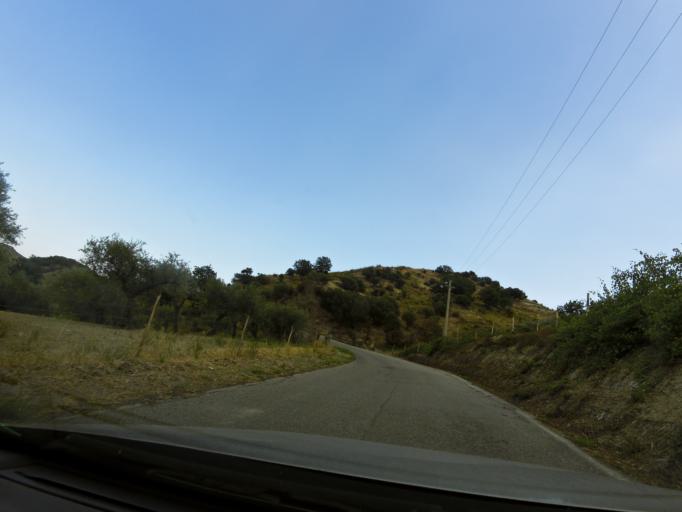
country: IT
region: Calabria
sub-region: Provincia di Reggio Calabria
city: Camini
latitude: 38.4606
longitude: 16.4958
